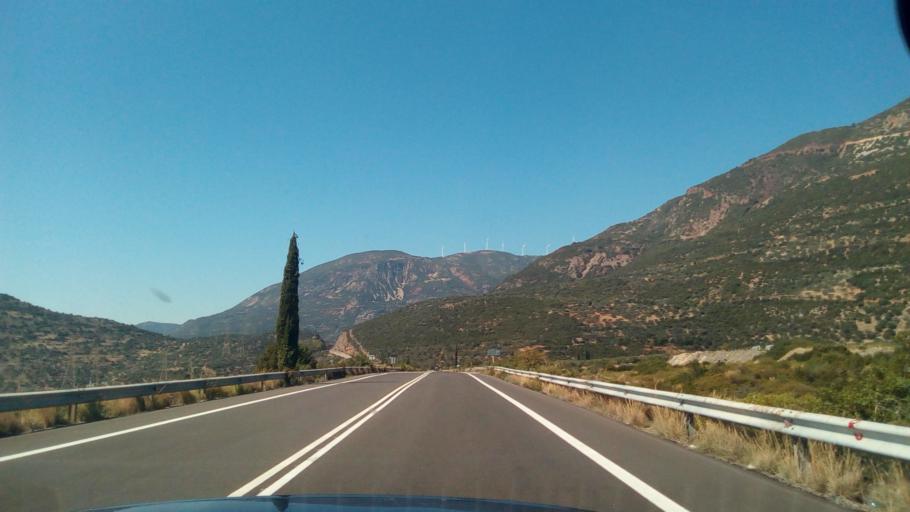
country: GR
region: West Greece
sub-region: Nomos Achaias
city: Selianitika
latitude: 38.3821
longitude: 22.0913
